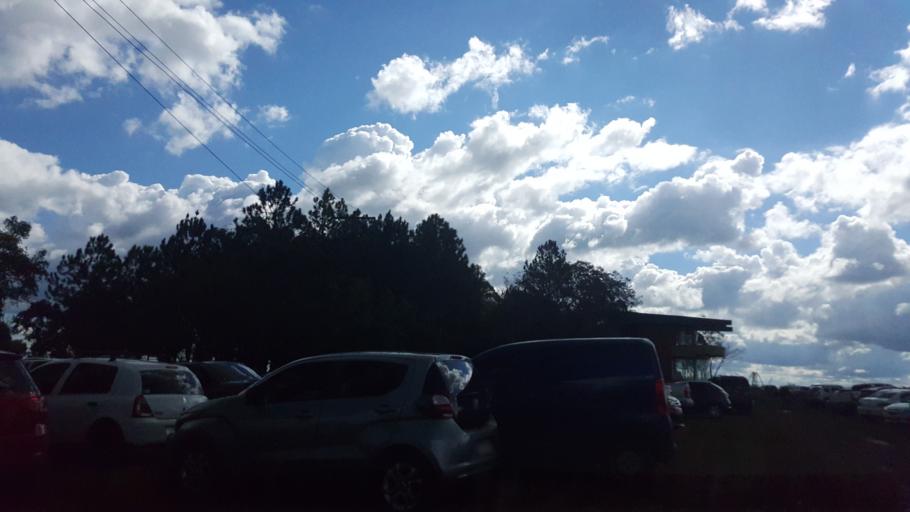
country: AR
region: Misiones
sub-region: Departamento de Capital
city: Posadas
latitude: -27.4176
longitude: -56.0070
